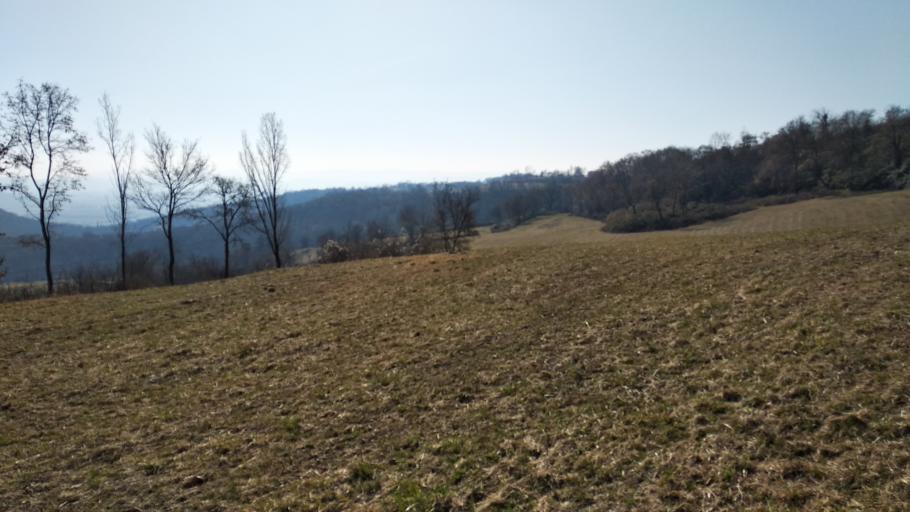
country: IT
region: Veneto
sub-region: Provincia di Vicenza
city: Gambugliano
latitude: 45.5934
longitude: 11.4558
